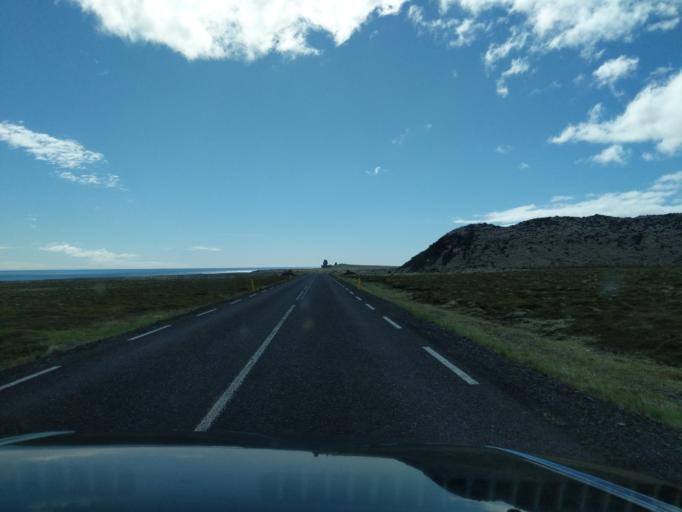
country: IS
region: West
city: Olafsvik
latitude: 64.7460
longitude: -23.7336
